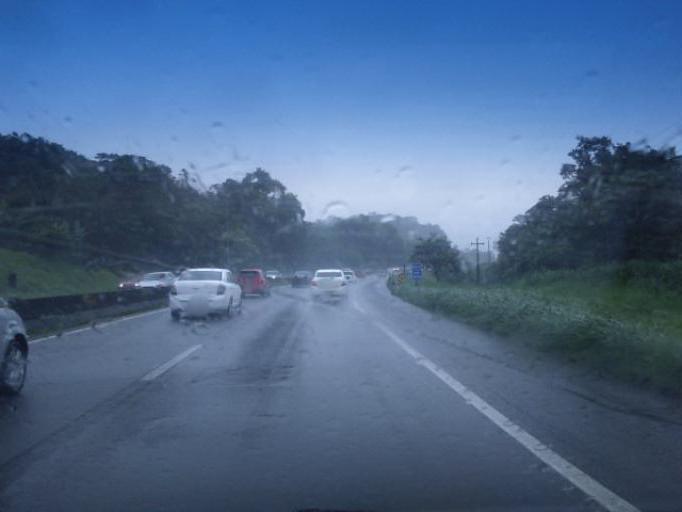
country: BR
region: Parana
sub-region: Guaratuba
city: Guaratuba
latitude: -25.9494
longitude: -48.9060
